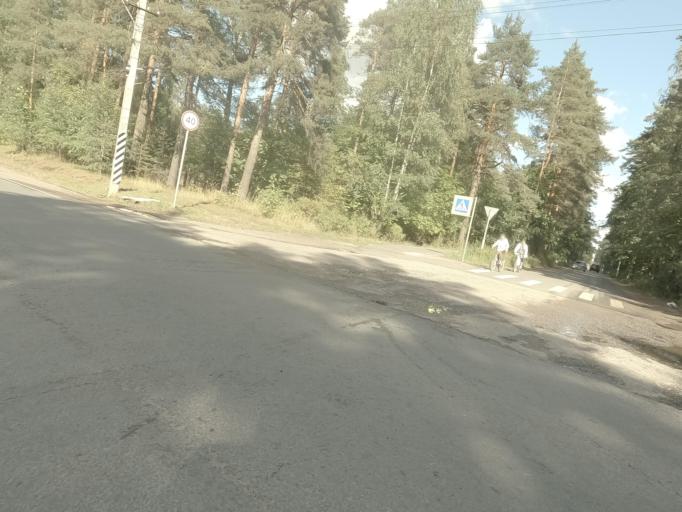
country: RU
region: Leningrad
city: Vsevolozhsk
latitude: 60.0081
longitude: 30.6650
